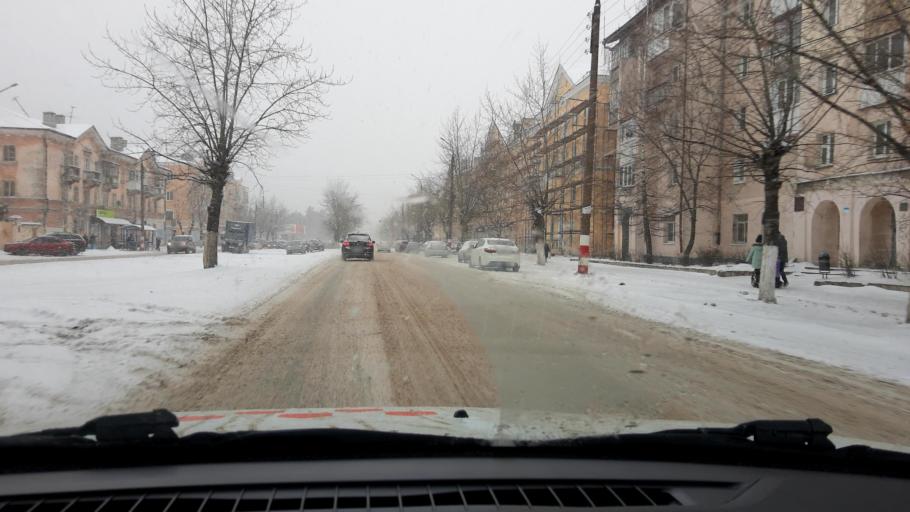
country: RU
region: Nizjnij Novgorod
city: Dzerzhinsk
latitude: 56.2394
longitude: 43.4801
